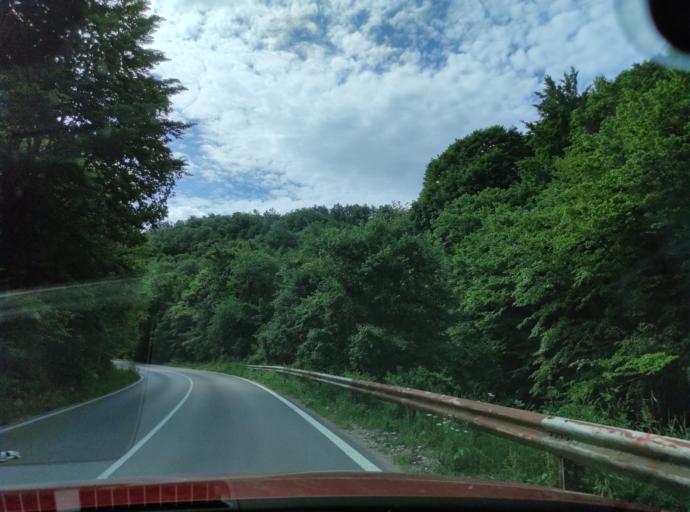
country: BG
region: Montana
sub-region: Obshtina Chiprovtsi
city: Chiprovtsi
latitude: 43.4640
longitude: 22.8810
